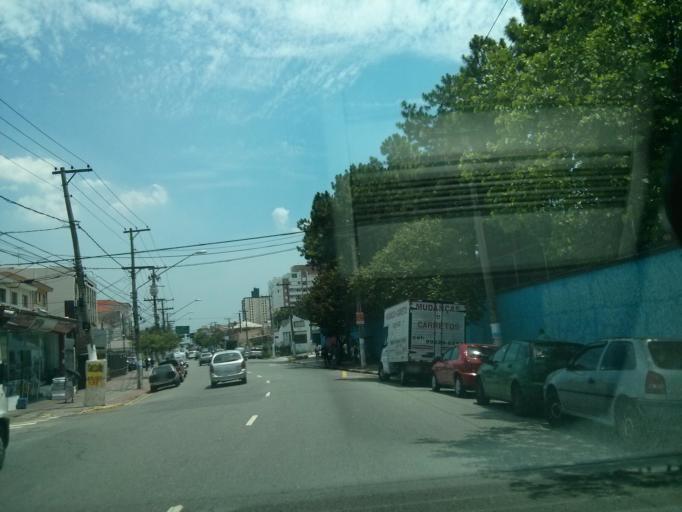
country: BR
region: Sao Paulo
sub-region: Sao Paulo
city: Sao Paulo
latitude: -23.6042
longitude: -46.6157
